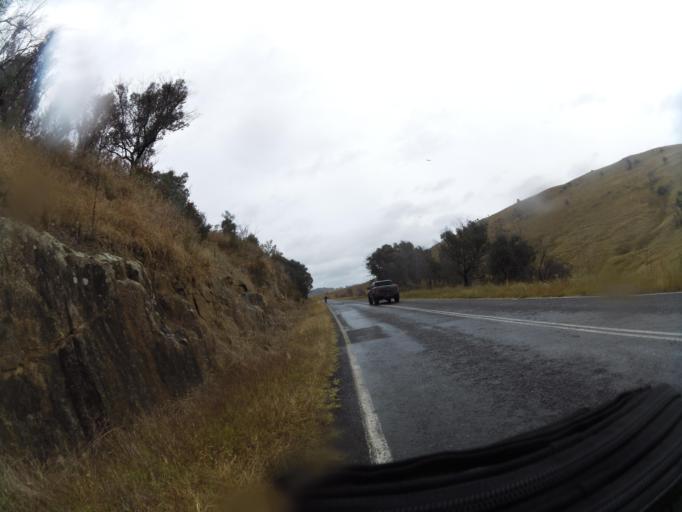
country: AU
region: New South Wales
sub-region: Greater Hume Shire
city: Holbrook
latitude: -36.2245
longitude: 147.7254
